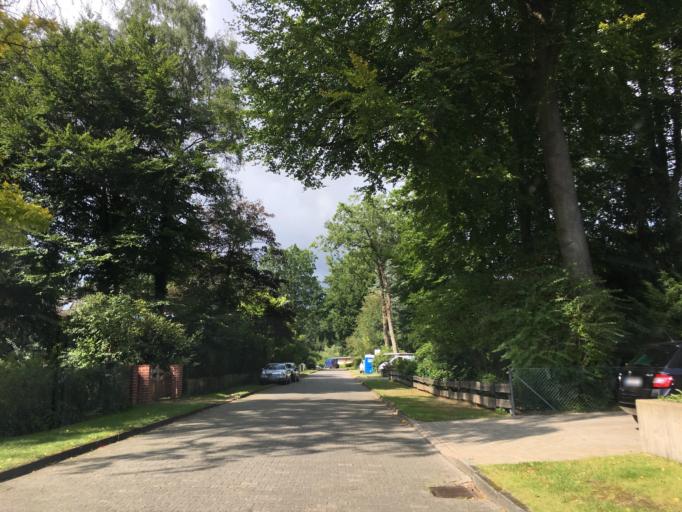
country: DE
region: Lower Saxony
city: Melbeck
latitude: 53.2153
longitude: 10.3956
